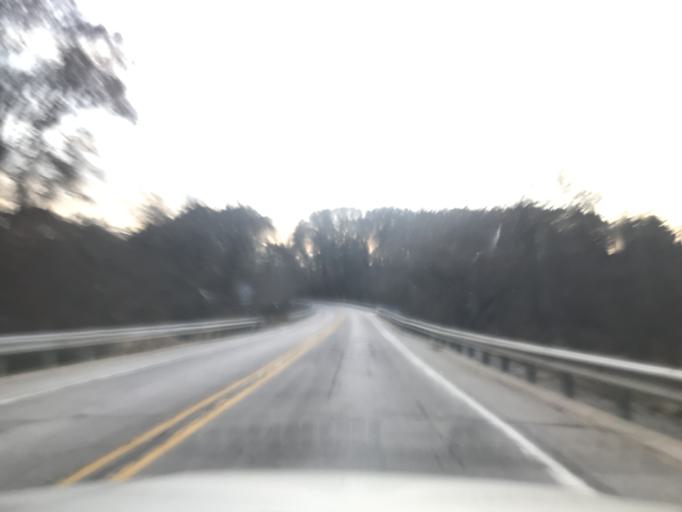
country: US
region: Illinois
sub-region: Henderson County
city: Oquawka
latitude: 40.9879
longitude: -90.8617
